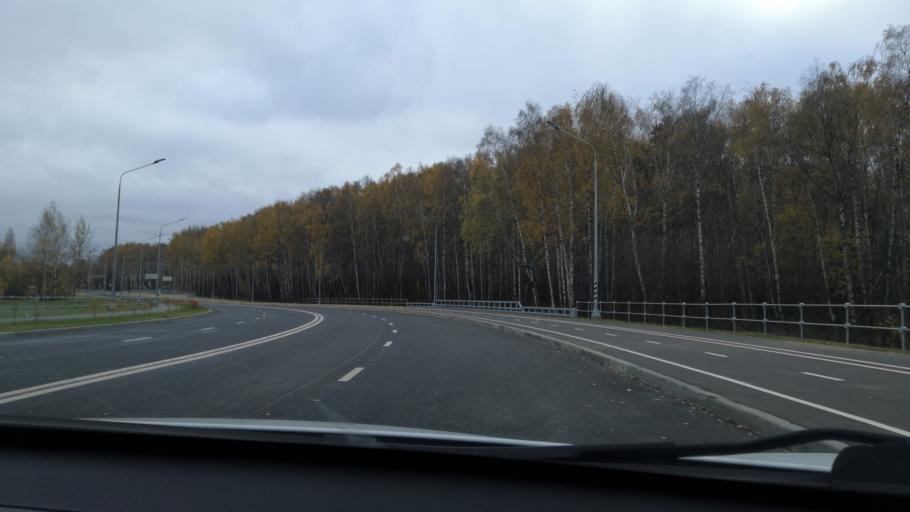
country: RU
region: Moscow
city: Severnyy
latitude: 55.9360
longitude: 37.5266
